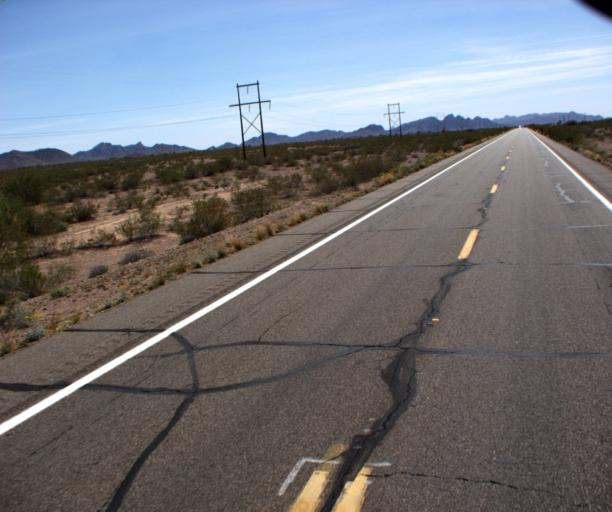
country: US
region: Arizona
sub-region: La Paz County
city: Quartzsite
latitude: 33.3872
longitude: -114.2172
